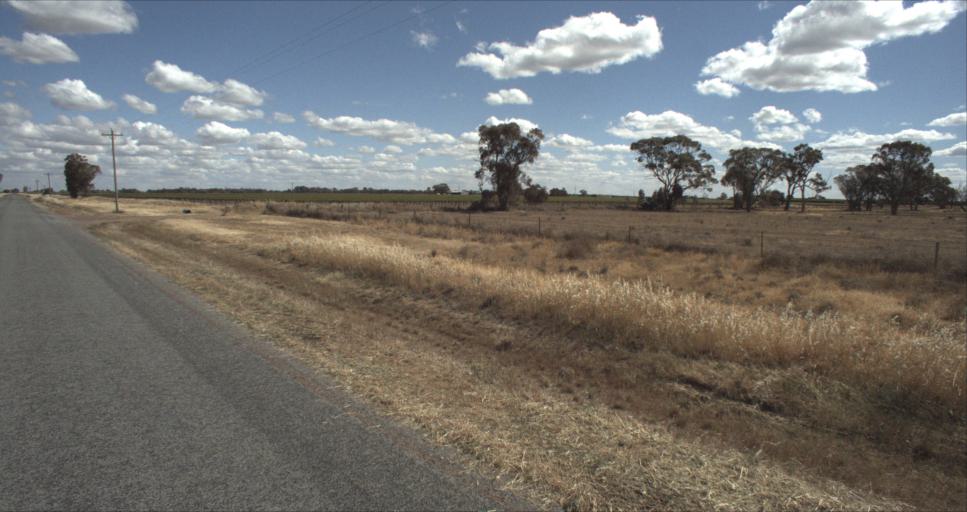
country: AU
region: New South Wales
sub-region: Leeton
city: Leeton
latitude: -34.4916
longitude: 146.2471
